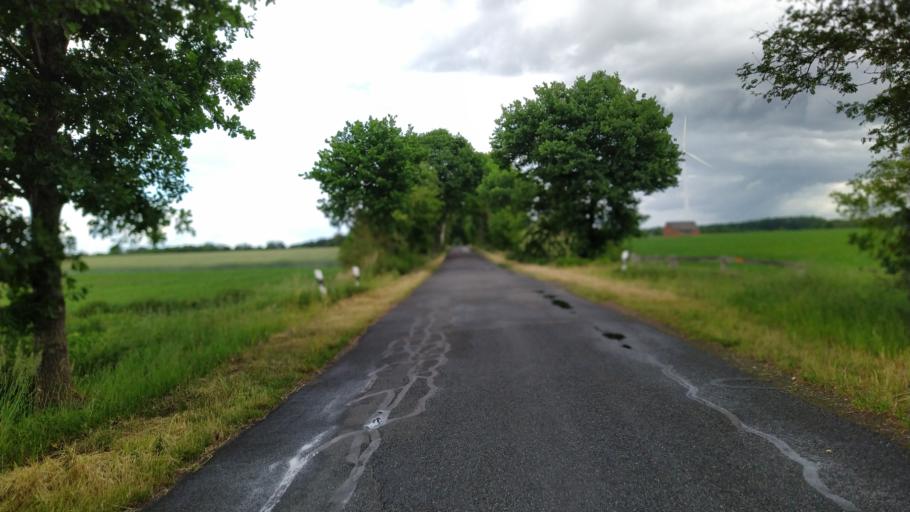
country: DE
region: Lower Saxony
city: Sandbostel
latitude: 53.4195
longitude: 9.1624
